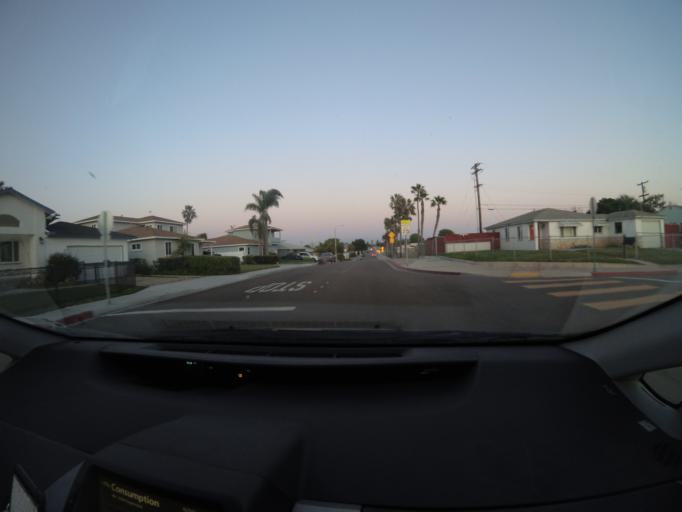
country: US
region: California
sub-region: San Diego County
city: Imperial Beach
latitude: 32.5803
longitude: -117.1253
